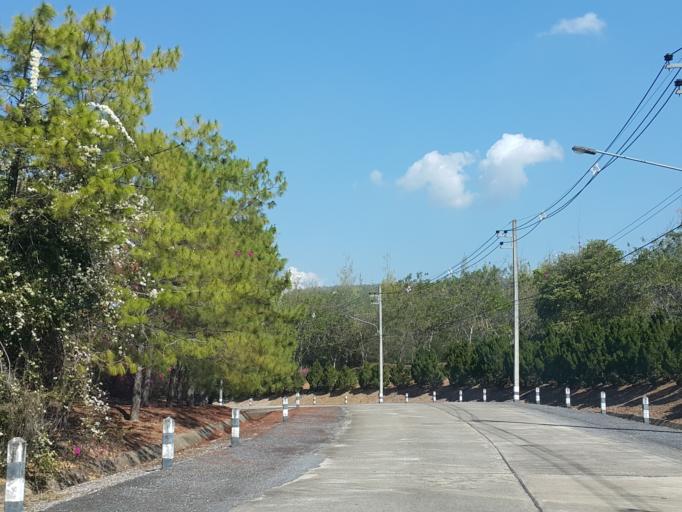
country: TH
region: Chiang Mai
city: Mae Taeng
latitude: 19.0248
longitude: 98.9895
